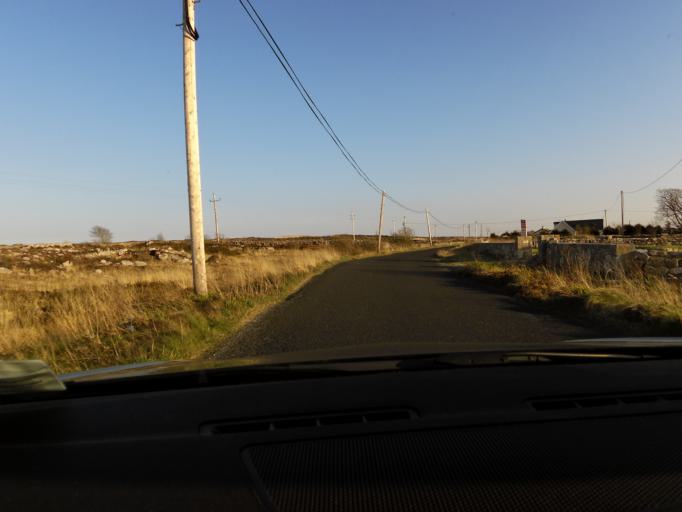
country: IE
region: Connaught
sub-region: County Galway
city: Oughterard
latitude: 53.2597
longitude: -9.5446
